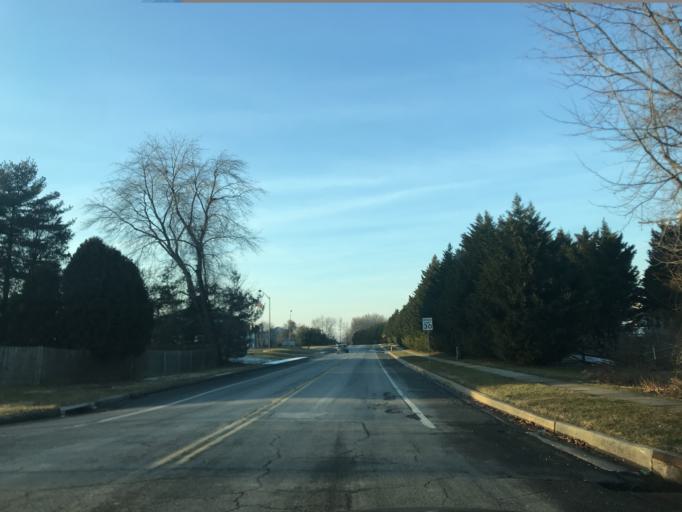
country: US
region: Maryland
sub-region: Harford County
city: Edgewood
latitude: 39.4317
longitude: -76.2695
